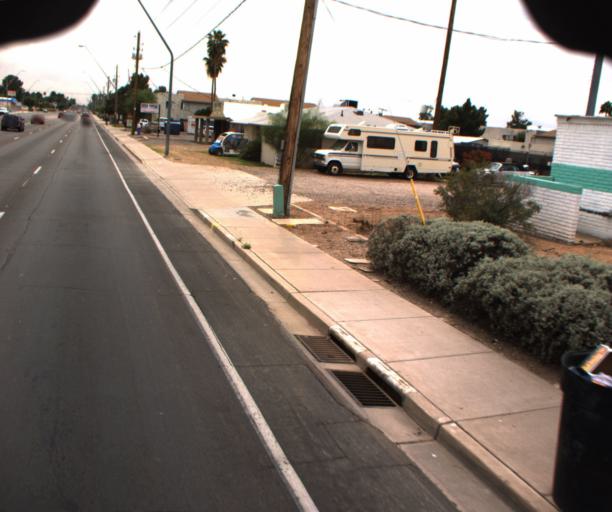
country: US
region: Arizona
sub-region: Maricopa County
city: Mesa
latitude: 33.4494
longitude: -111.8399
